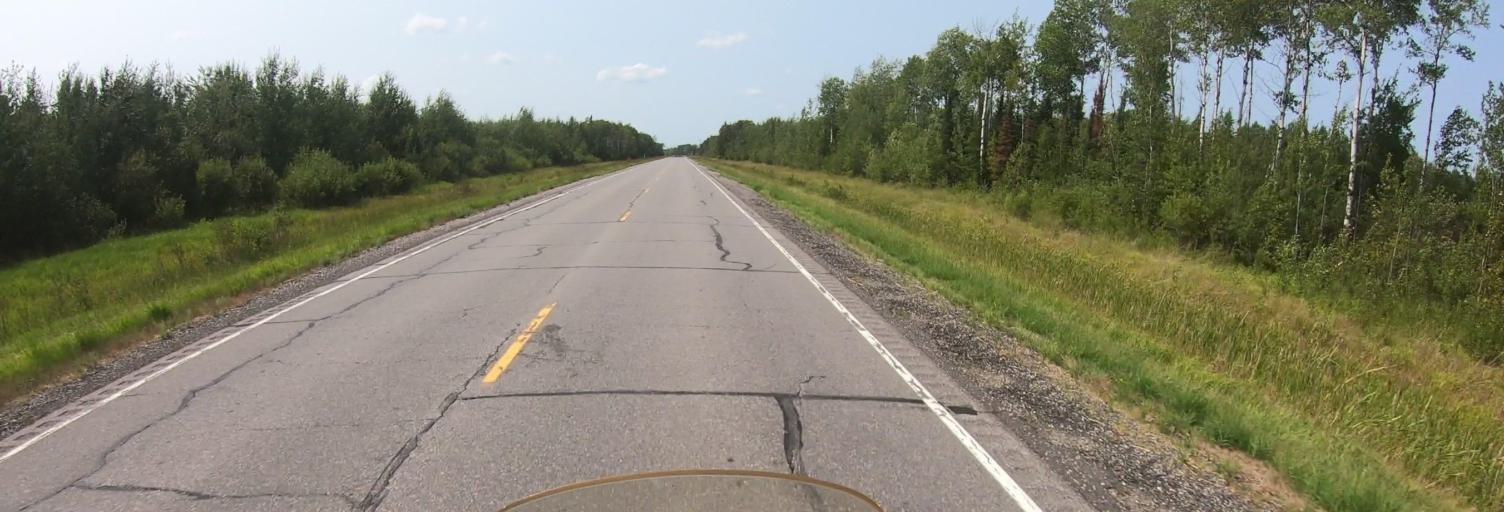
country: US
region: Minnesota
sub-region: Lake of the Woods County
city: Baudette
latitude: 48.6996
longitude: -94.3979
